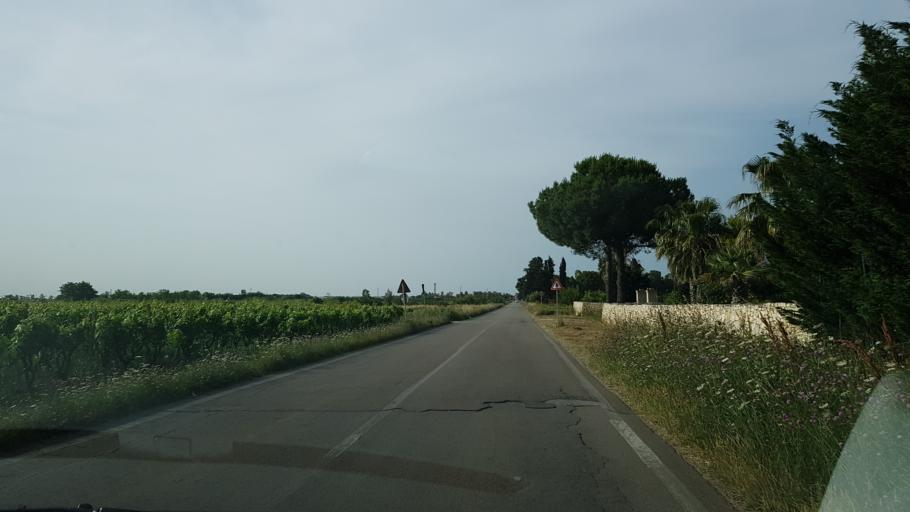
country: IT
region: Apulia
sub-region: Provincia di Brindisi
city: San Pancrazio Salentino
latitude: 40.4014
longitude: 17.8354
